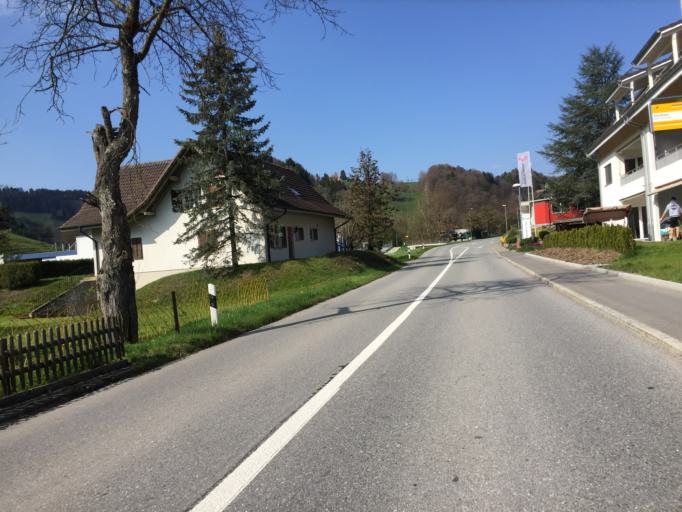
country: CH
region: Bern
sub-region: Bern-Mittelland District
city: Bariswil
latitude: 46.9991
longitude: 7.5405
